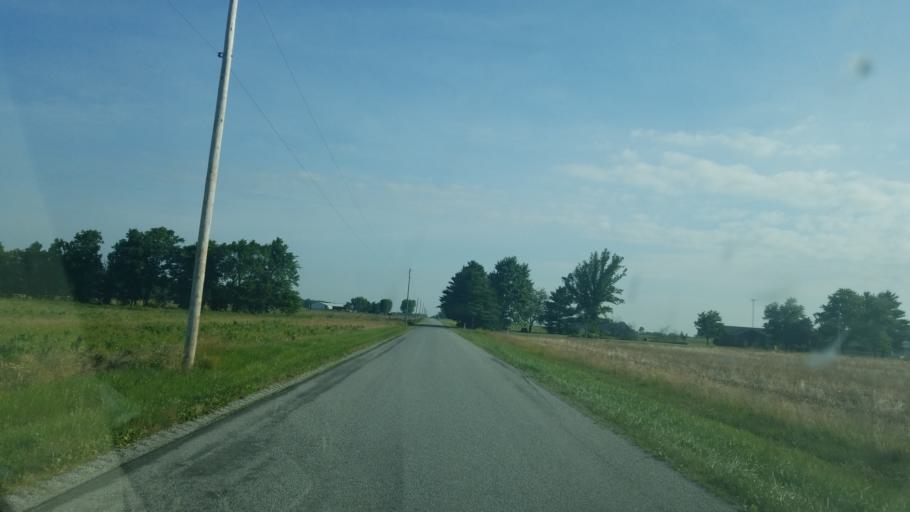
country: US
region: Ohio
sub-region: Hancock County
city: Arlington
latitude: 40.8040
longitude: -83.6706
